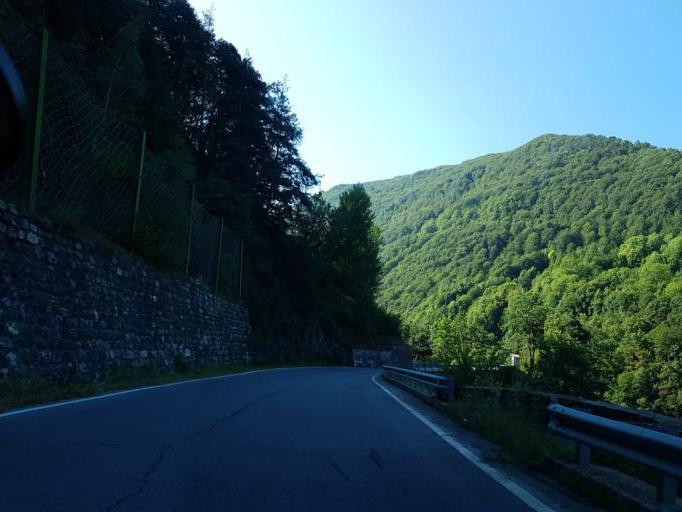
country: IT
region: Piedmont
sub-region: Provincia di Cuneo
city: San Damiano Macra
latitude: 44.4914
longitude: 7.2433
